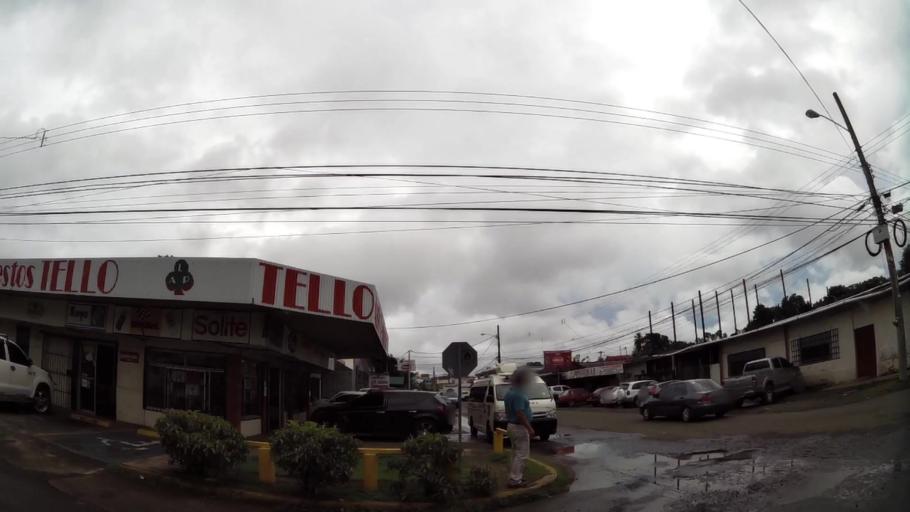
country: PA
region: Chiriqui
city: David
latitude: 8.4348
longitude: -82.4260
